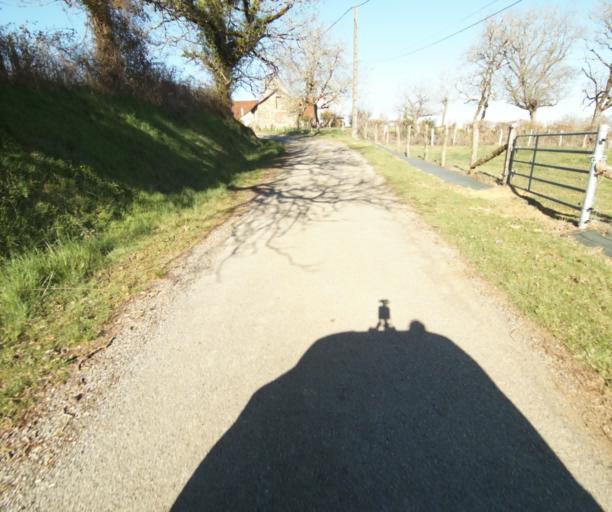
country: FR
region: Limousin
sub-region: Departement de la Correze
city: Seilhac
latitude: 45.3879
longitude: 1.7297
